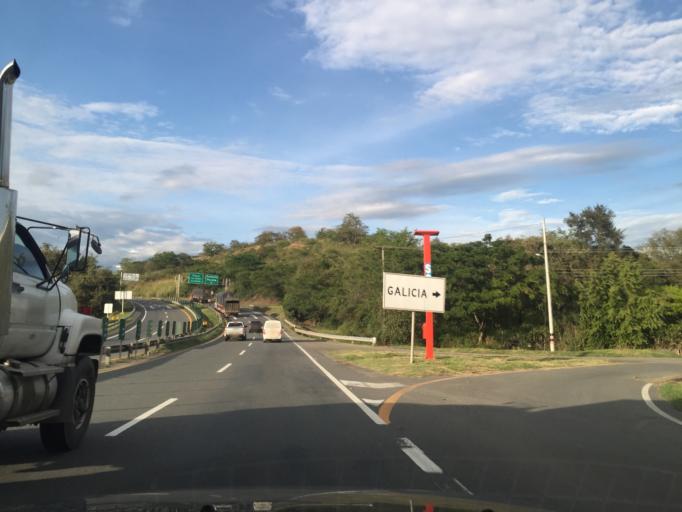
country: CO
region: Valle del Cauca
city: Bugalagrande
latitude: 4.2009
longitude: -76.1539
